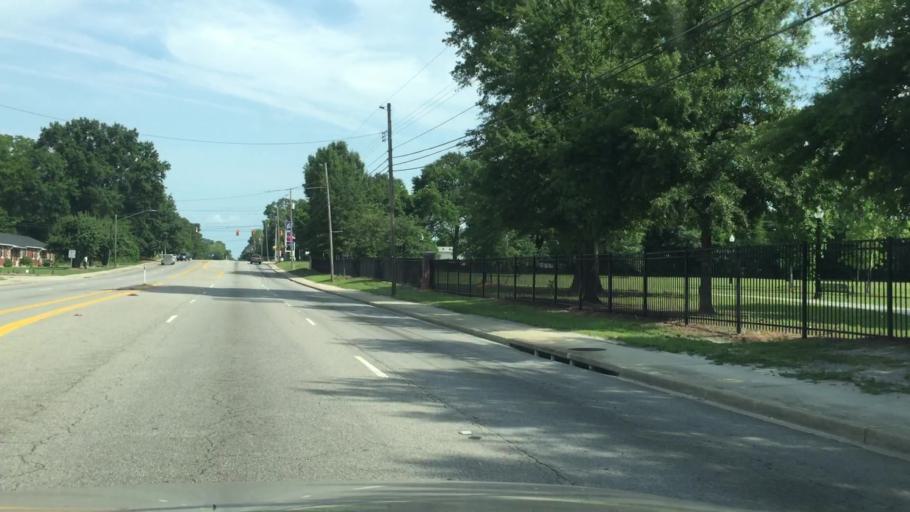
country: US
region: South Carolina
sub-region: Sumter County
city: South Sumter
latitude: 33.9139
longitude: -80.3552
